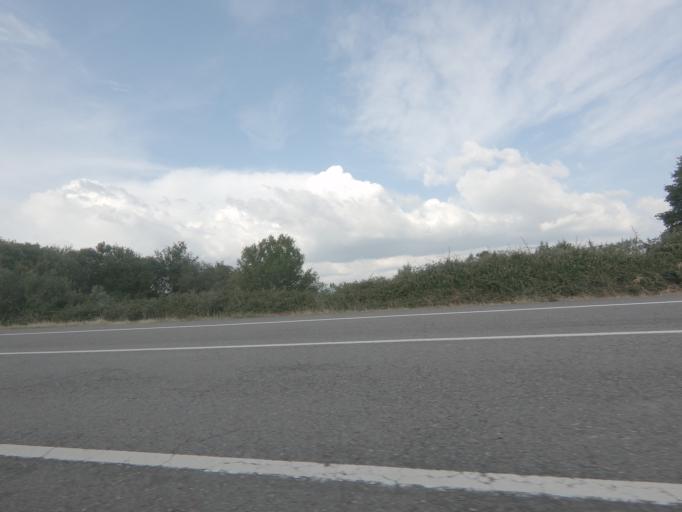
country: ES
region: Galicia
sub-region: Provincia de Ourense
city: Ambia
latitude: 42.1540
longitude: -7.7574
